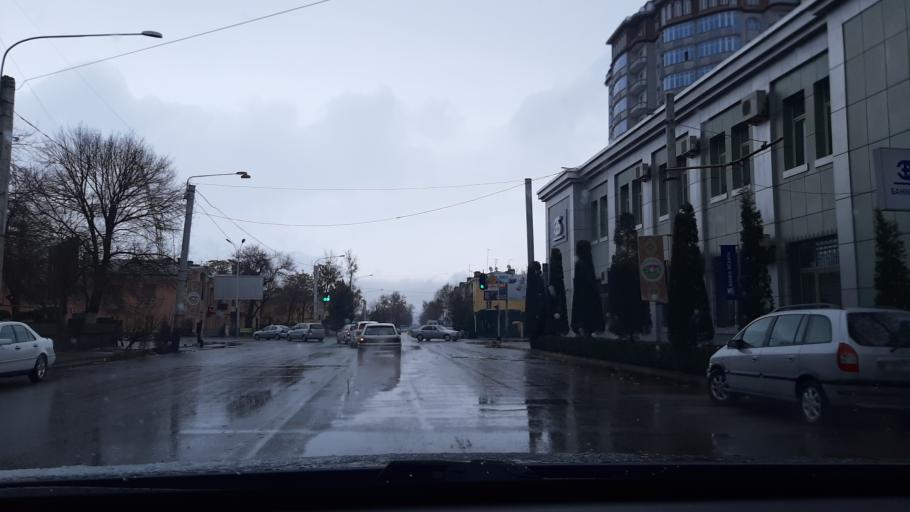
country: TJ
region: Viloyati Sughd
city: Khujand
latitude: 40.2772
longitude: 69.6410
